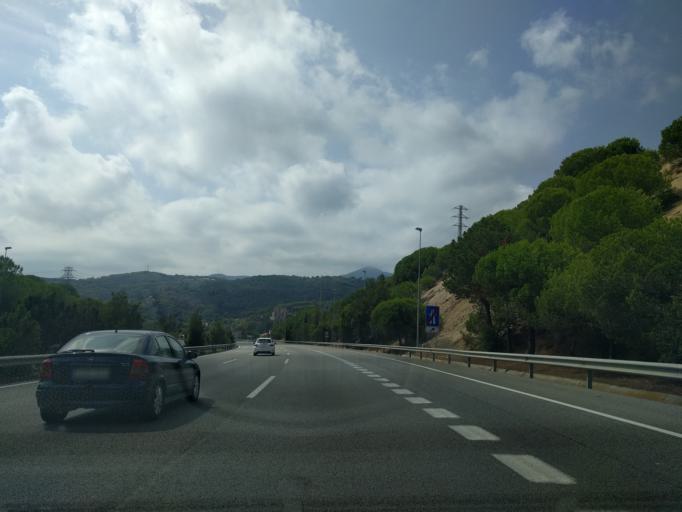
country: ES
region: Catalonia
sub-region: Provincia de Barcelona
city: Arenys de Mar
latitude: 41.5917
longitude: 2.5483
